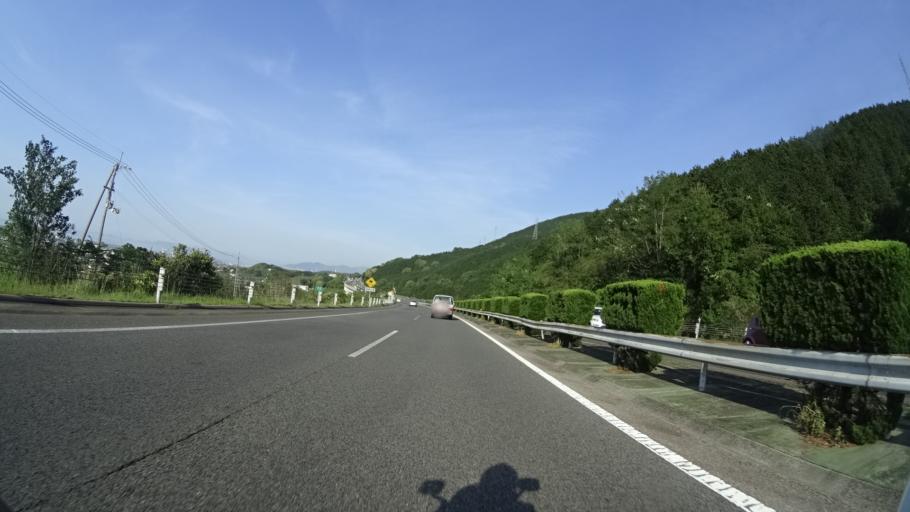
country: JP
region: Ehime
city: Niihama
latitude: 33.9456
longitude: 133.4123
